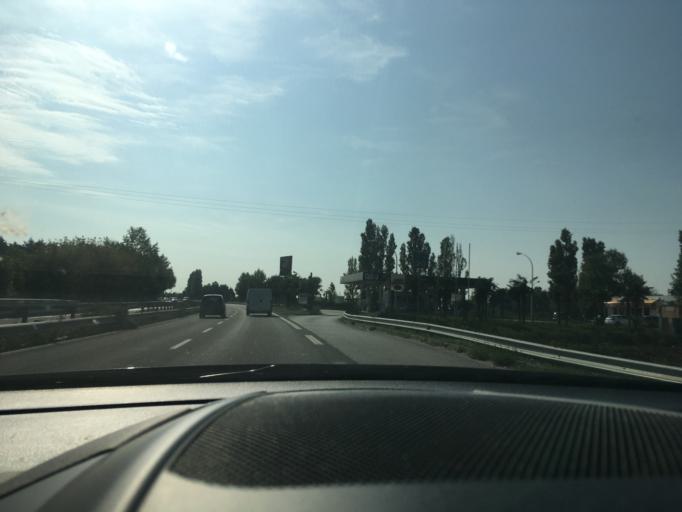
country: IT
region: Emilia-Romagna
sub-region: Forli-Cesena
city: San Mauro a Mare
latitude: 44.1505
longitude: 12.4435
